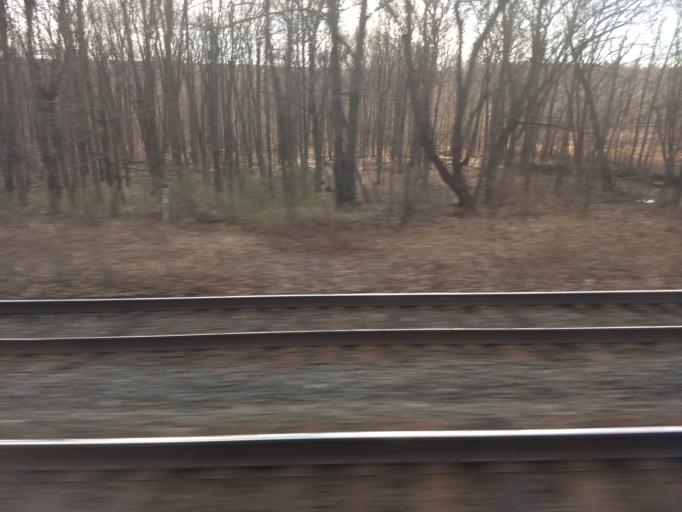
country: US
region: Pennsylvania
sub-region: Blair County
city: Bellwood
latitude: 40.5843
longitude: -78.3475
